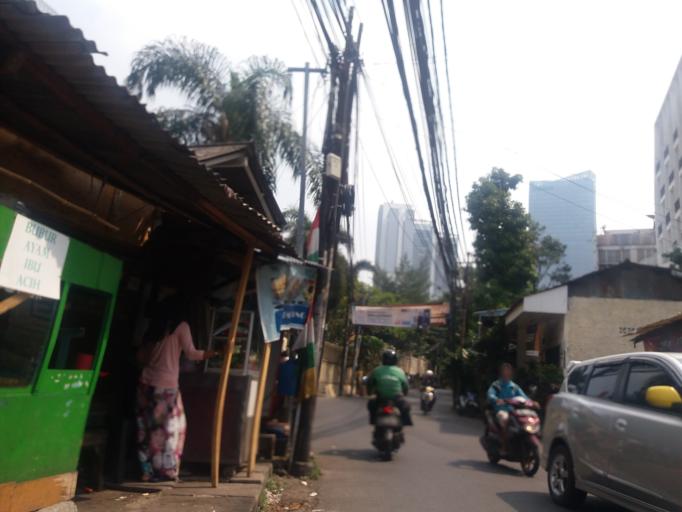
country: ID
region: Jakarta Raya
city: Jakarta
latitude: -6.2212
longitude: 106.8246
